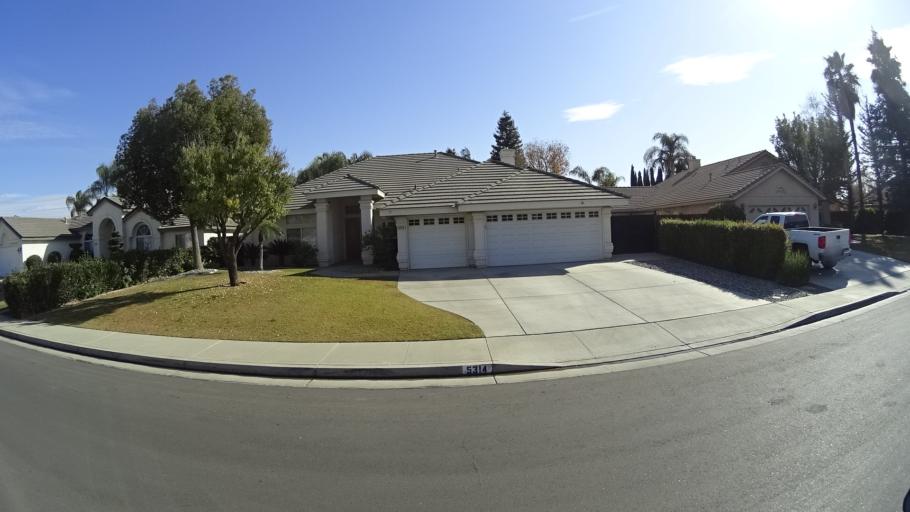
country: US
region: California
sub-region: Kern County
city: Greenacres
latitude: 35.4082
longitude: -119.0944
